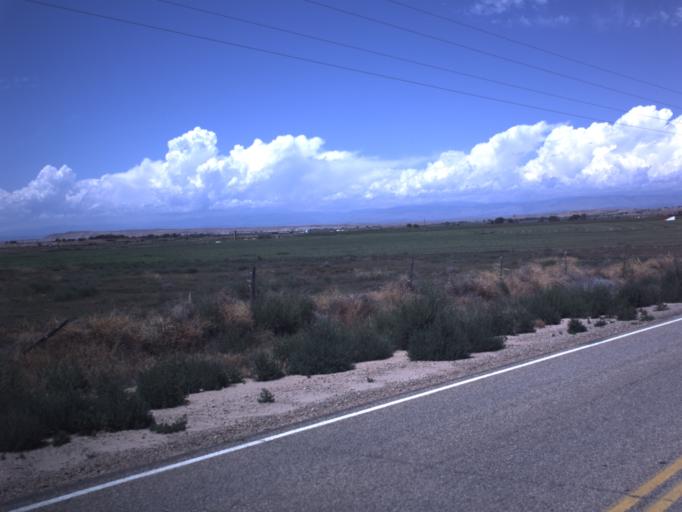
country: US
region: Utah
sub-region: Uintah County
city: Naples
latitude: 40.1677
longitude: -109.6644
